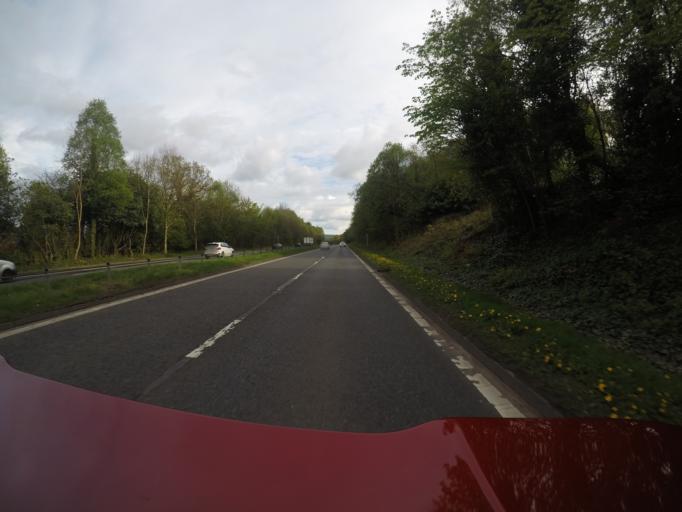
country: GB
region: Scotland
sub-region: West Dunbartonshire
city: Renton
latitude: 55.9684
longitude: -4.5877
